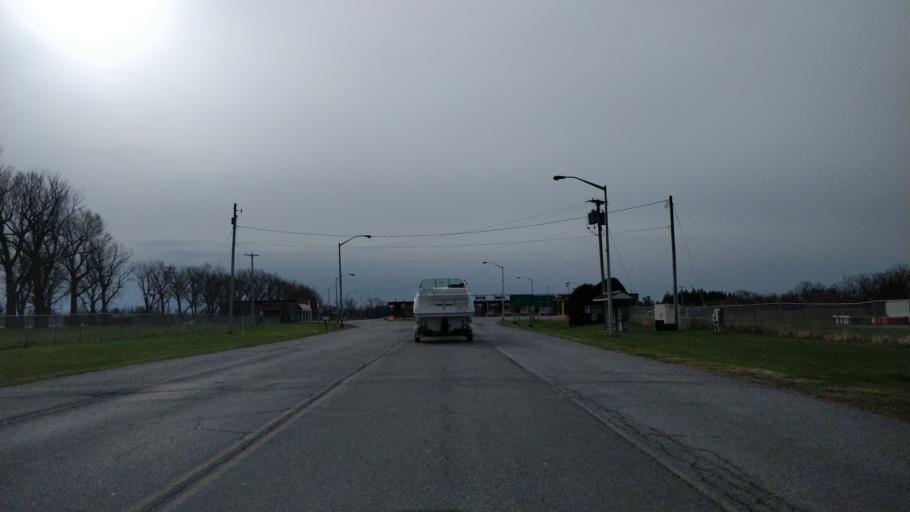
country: US
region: New York
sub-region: St. Lawrence County
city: Ogdensburg
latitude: 44.7245
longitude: -75.4549
